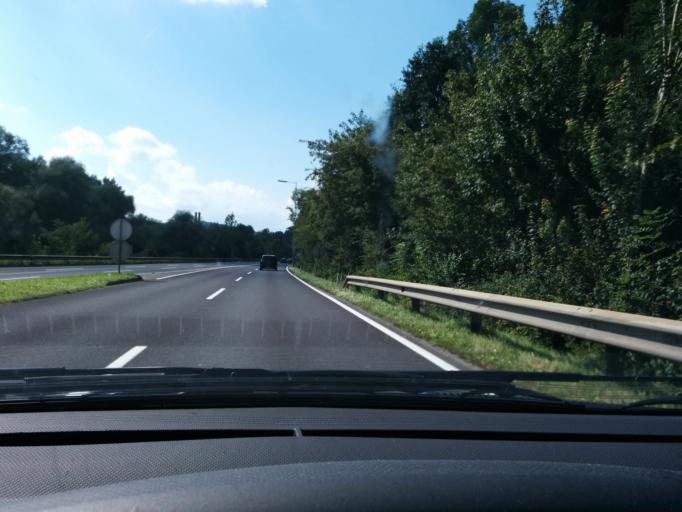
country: AT
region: Upper Austria
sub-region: Politischer Bezirk Linz-Land
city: Leonding
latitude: 48.3114
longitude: 14.2505
